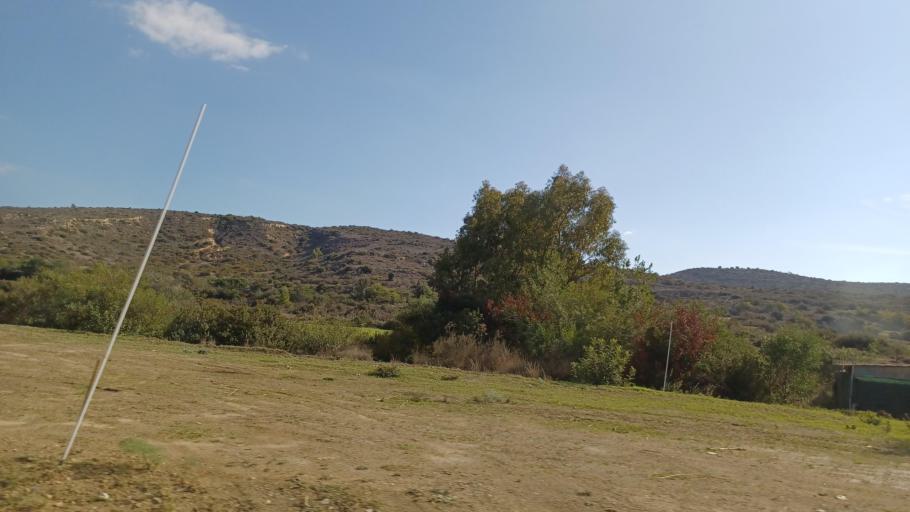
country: CY
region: Limassol
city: Pyrgos
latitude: 34.7281
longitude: 33.2063
